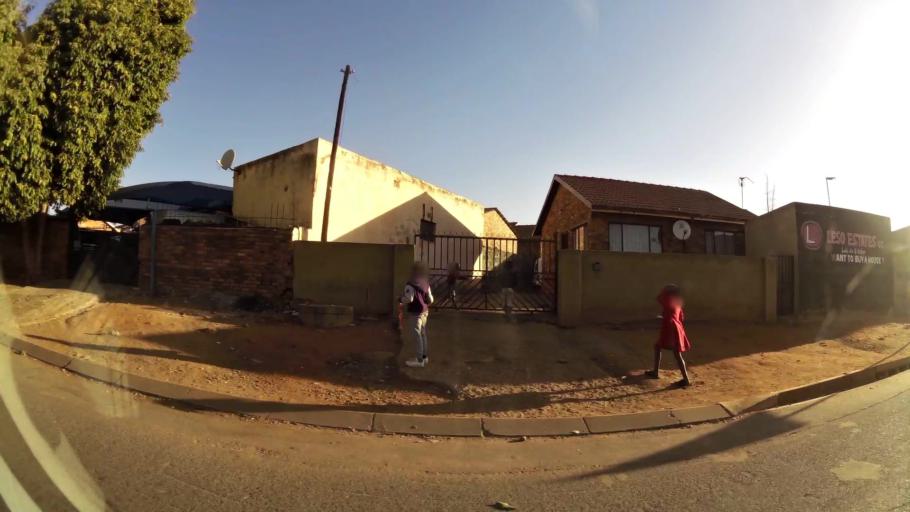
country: ZA
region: Gauteng
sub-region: Ekurhuleni Metropolitan Municipality
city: Tembisa
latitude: -26.0109
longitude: 28.2313
